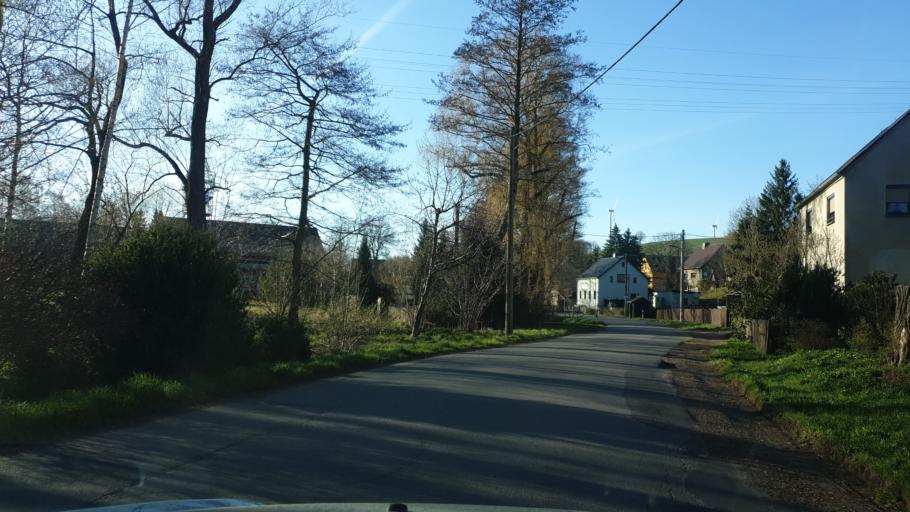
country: DE
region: Saxony
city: Kirchberg
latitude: 50.7647
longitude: 12.7300
